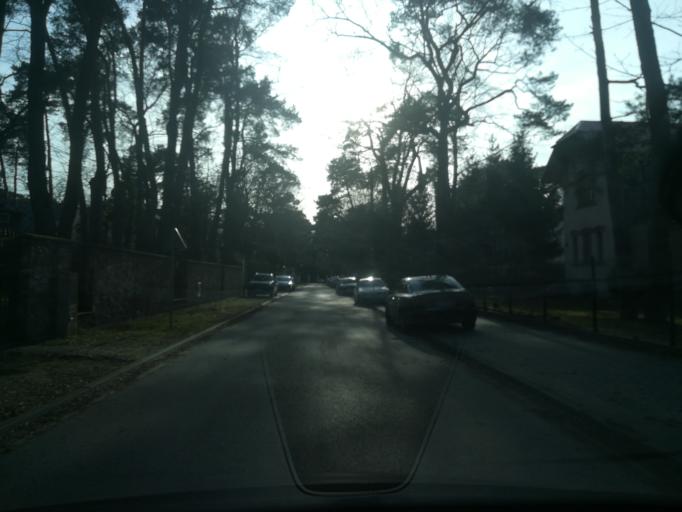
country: PL
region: Masovian Voivodeship
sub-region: Powiat piaseczynski
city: Konstancin-Jeziorna
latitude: 52.0858
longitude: 21.1236
